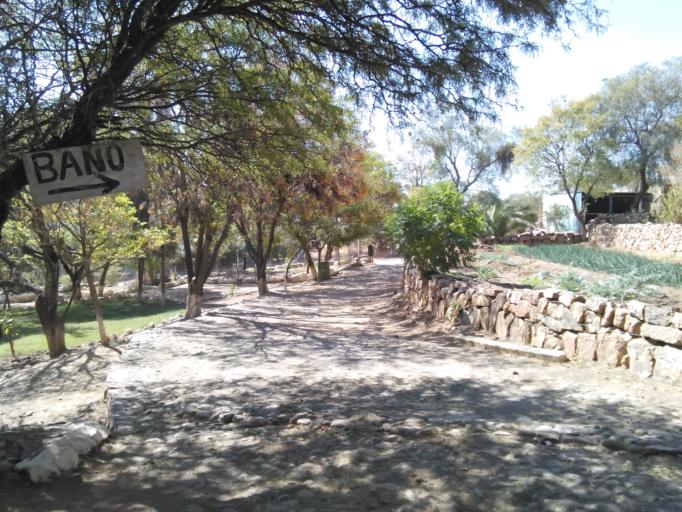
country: BO
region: Cochabamba
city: Sipe Sipe
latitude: -17.4213
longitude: -66.2833
